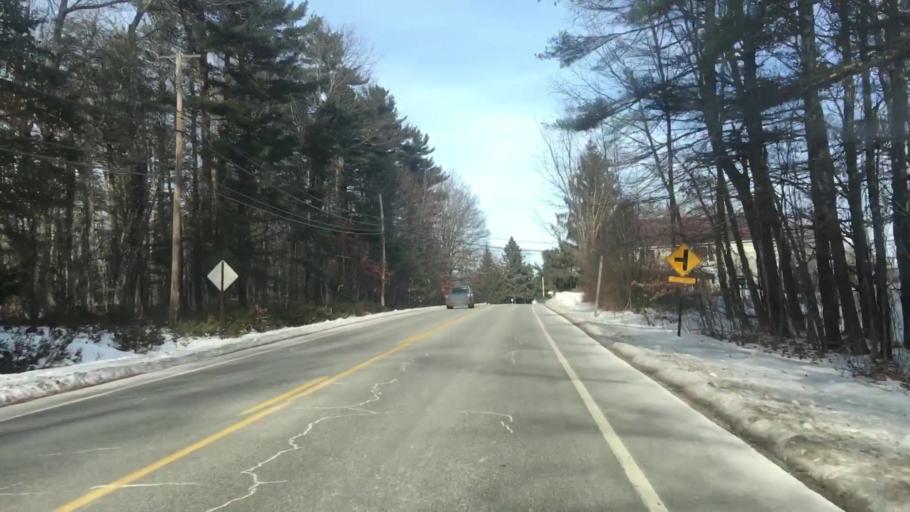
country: US
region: Maine
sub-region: Cumberland County
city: South Windham
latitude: 43.7689
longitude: -70.4210
